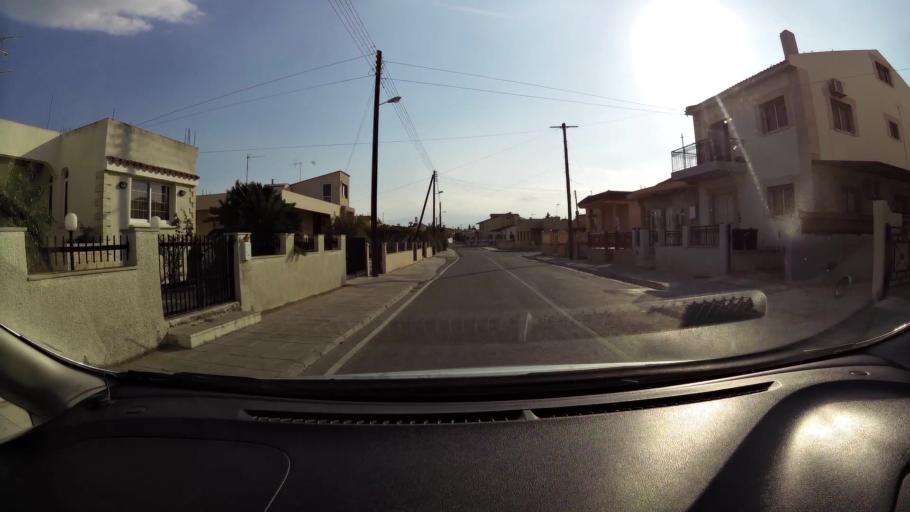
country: CY
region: Larnaka
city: Dhromolaxia
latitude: 34.8791
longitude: 33.5880
